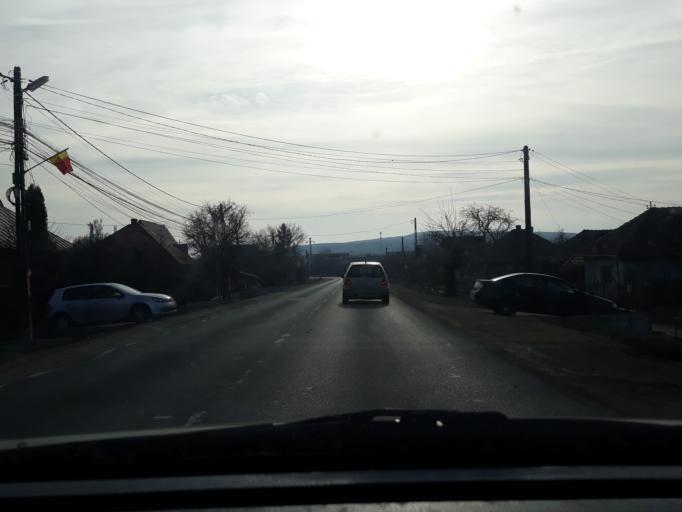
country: RO
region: Salaj
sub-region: Comuna Criseni
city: Criseni
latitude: 47.2293
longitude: 23.0415
